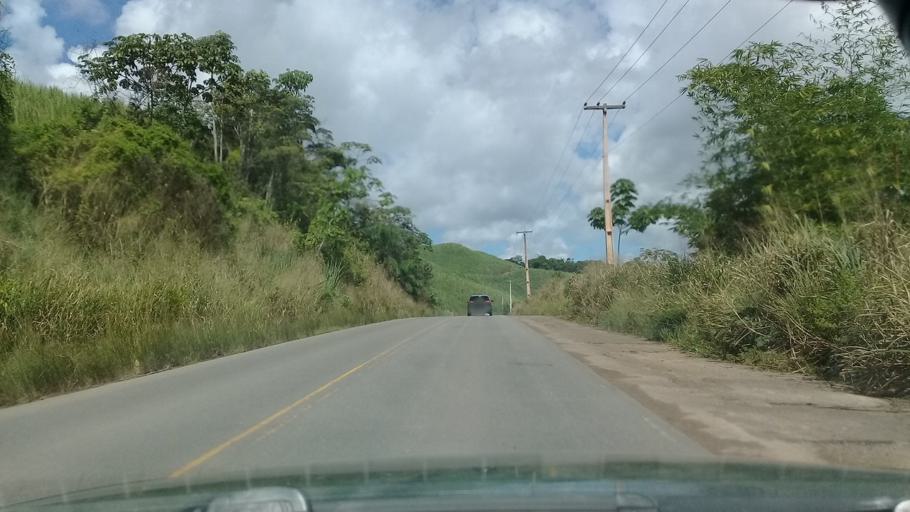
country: BR
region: Pernambuco
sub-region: Ipojuca
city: Ipojuca
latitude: -8.4502
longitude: -35.0947
